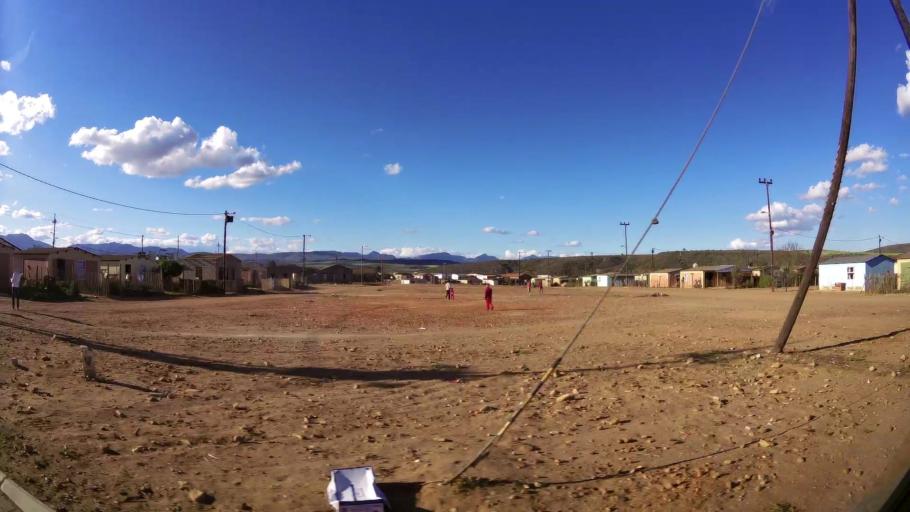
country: ZA
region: Western Cape
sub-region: Eden District Municipality
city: Riversdale
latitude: -34.1085
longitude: 20.9630
